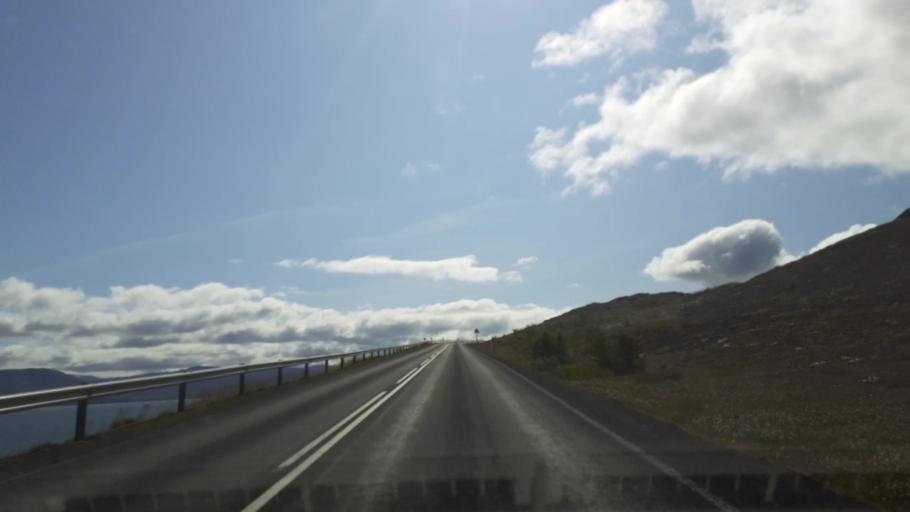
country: IS
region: Northeast
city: Akureyri
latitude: 65.8850
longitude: -18.2694
